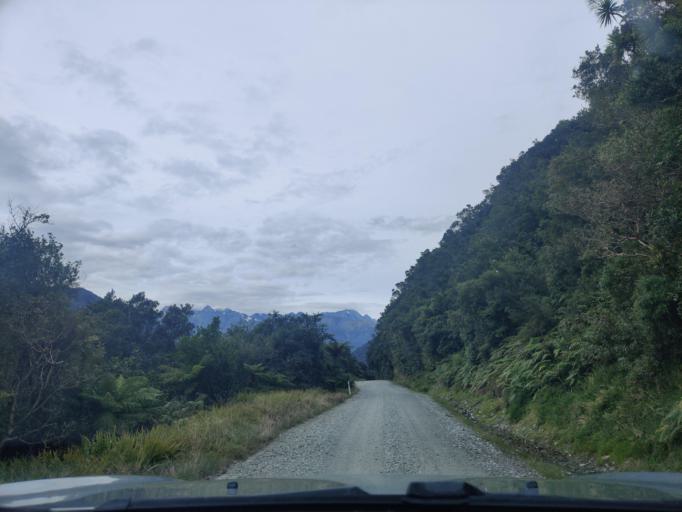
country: NZ
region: West Coast
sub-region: Westland District
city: Hokitika
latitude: -43.2882
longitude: 170.4046
